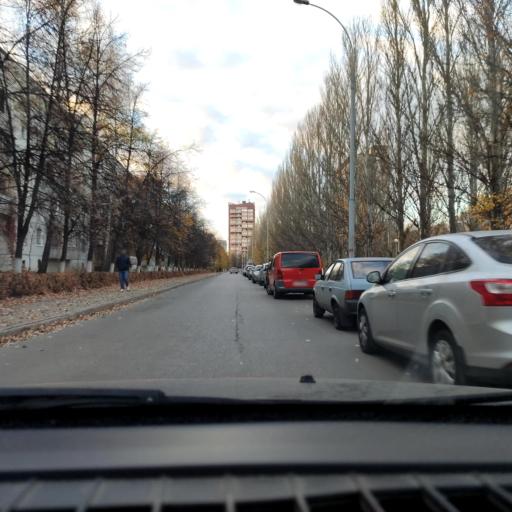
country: RU
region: Samara
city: Tol'yatti
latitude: 53.5301
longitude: 49.3042
